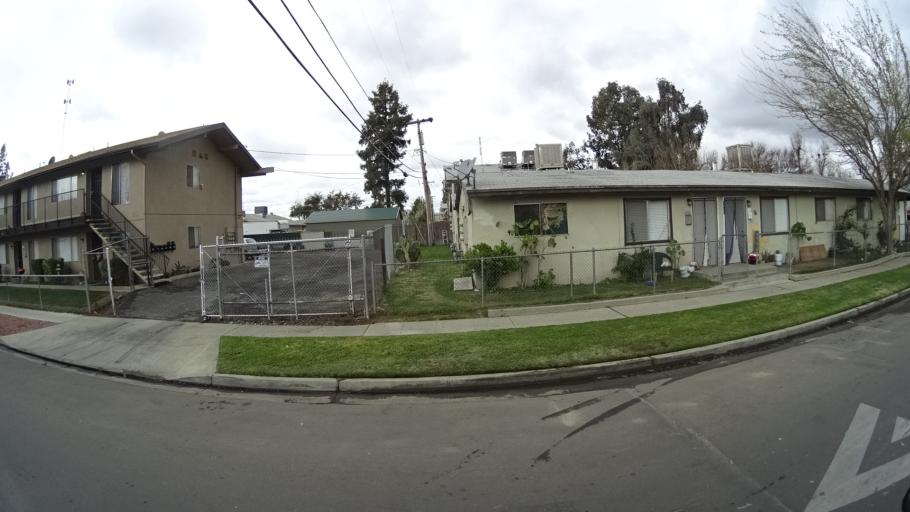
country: US
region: California
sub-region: Fresno County
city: West Park
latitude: 36.7806
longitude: -119.8400
